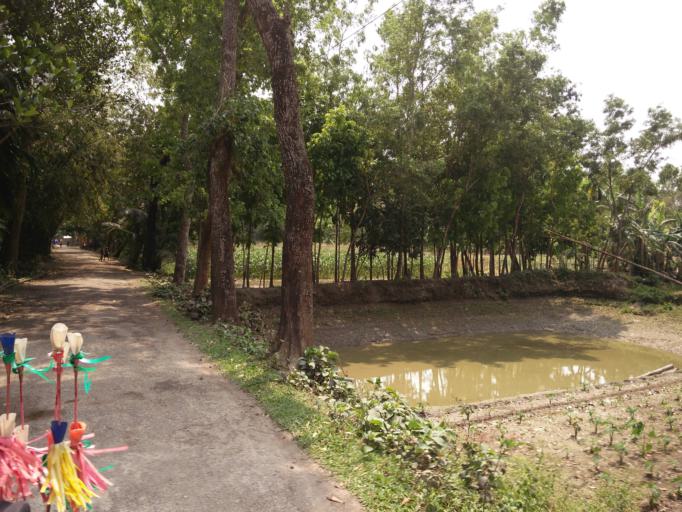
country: BD
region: Dhaka
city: Sherpur
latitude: 24.9285
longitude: 90.1683
